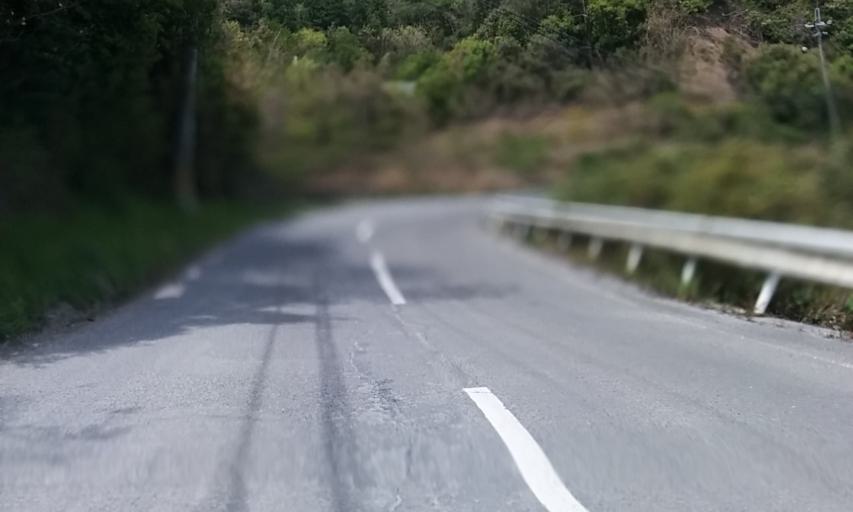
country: JP
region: Osaka
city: Takatsuki
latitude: 34.9143
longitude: 135.5992
